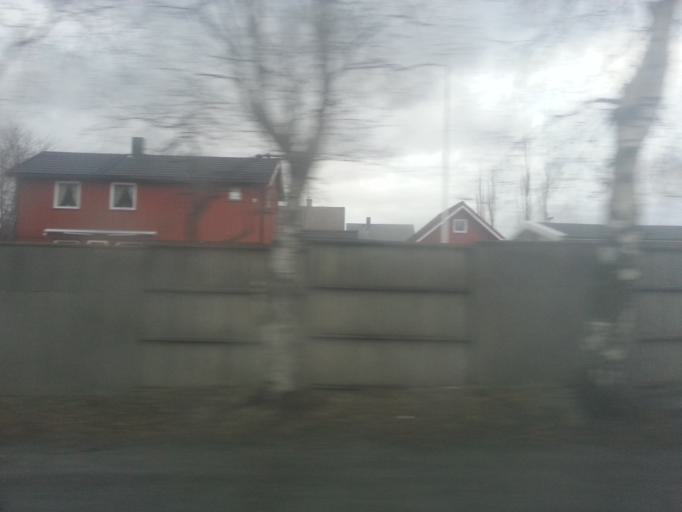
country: NO
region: Sor-Trondelag
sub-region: Trondheim
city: Trondheim
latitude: 63.4318
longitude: 10.4553
